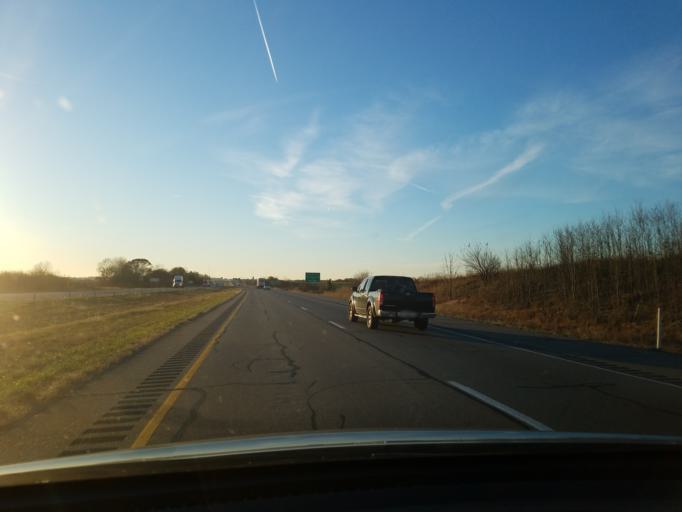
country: US
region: Indiana
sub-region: Gibson County
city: Haubstadt
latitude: 38.1671
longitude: -87.5333
